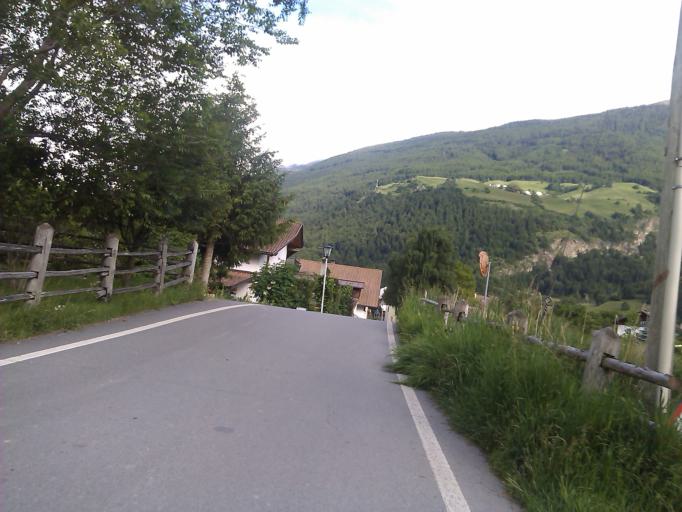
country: IT
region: Trentino-Alto Adige
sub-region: Bolzano
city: Lasa
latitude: 46.6163
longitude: 10.6939
